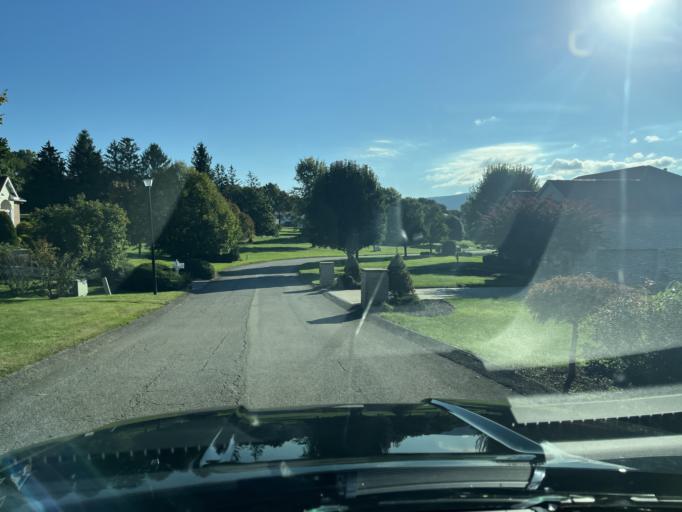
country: US
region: Pennsylvania
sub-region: Fayette County
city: Leith-Hatfield
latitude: 39.8761
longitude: -79.7371
